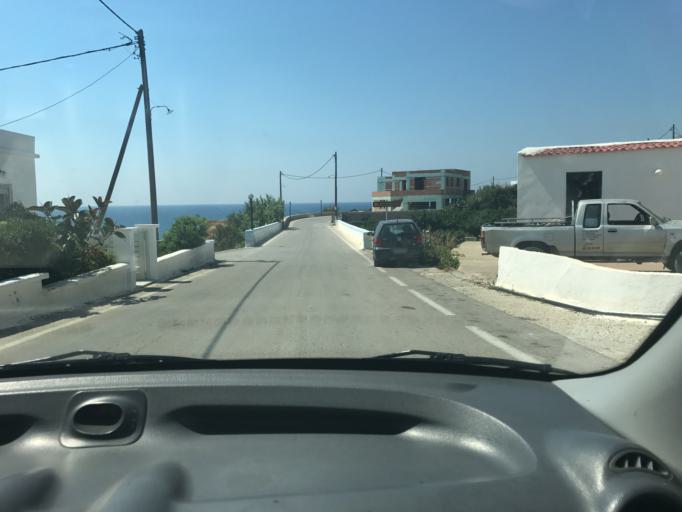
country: GR
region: South Aegean
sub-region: Nomos Dodekanisou
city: Karpathos
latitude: 35.4760
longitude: 27.1179
